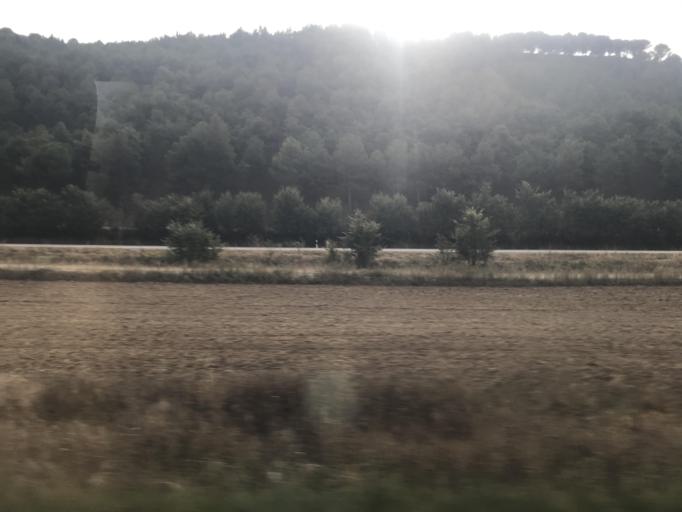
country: ES
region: Castille and Leon
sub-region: Provincia de Burgos
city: Pradanos de Bureba
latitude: 42.5191
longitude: -3.3360
